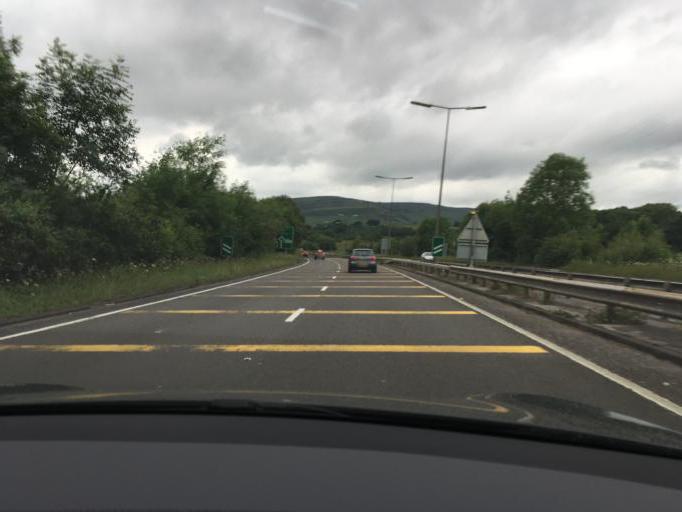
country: GB
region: England
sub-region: Derbyshire
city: Chapel en le Frith
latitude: 53.3294
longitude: -1.9044
